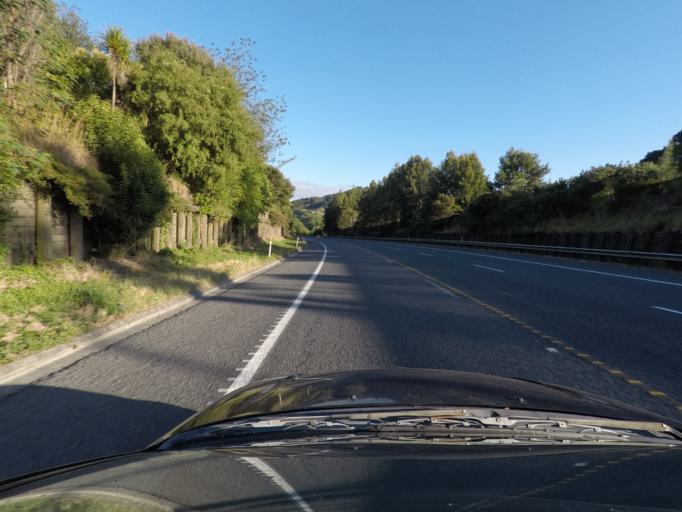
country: NZ
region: Northland
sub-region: Whangarei
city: Whangarei
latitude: -35.6290
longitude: 174.2959
